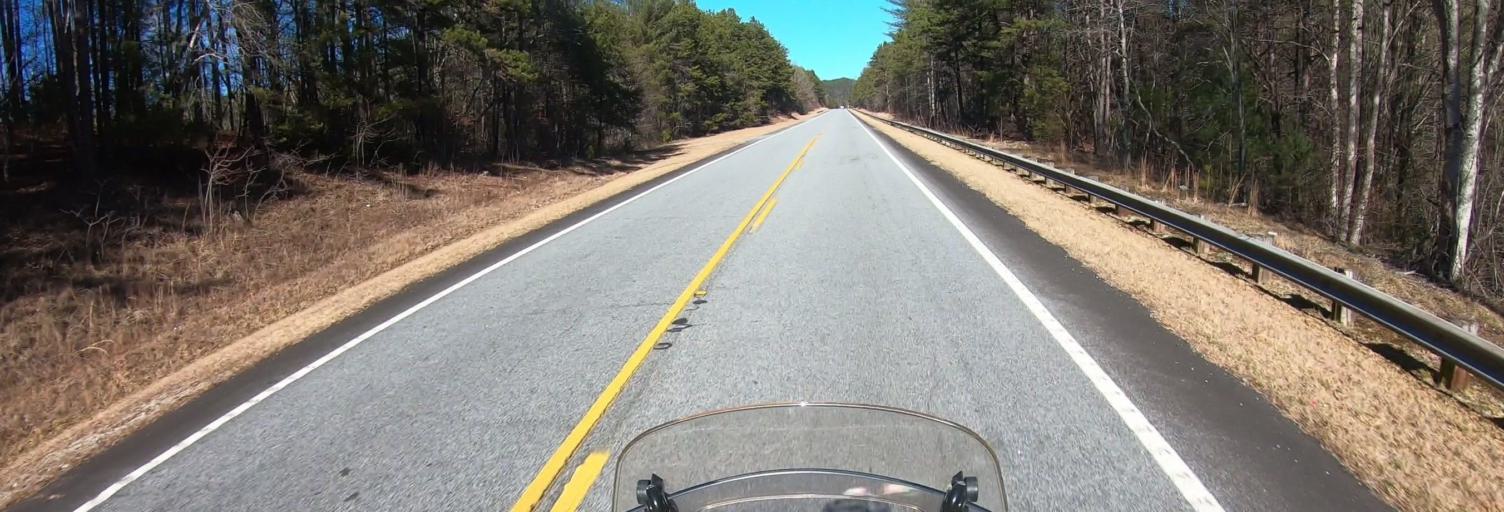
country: US
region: South Carolina
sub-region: Pickens County
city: Pickens
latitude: 34.9509
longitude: -82.8518
